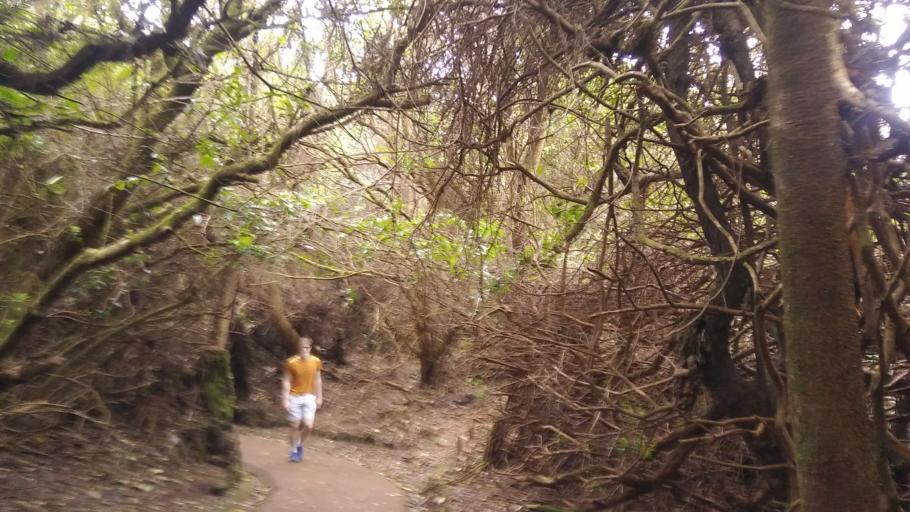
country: CR
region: Alajuela
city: Rio Segundo
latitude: 10.1897
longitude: -84.2292
